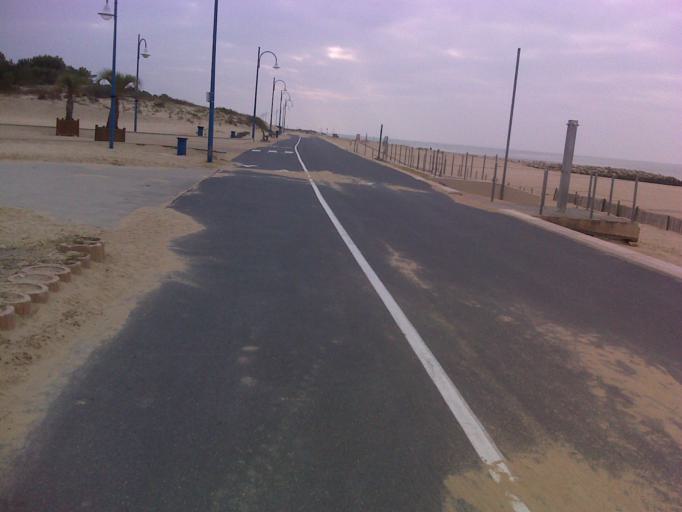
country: FR
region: Poitou-Charentes
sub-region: Departement de la Charente-Maritime
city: Les Mathes
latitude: 45.6816
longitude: -1.1789
